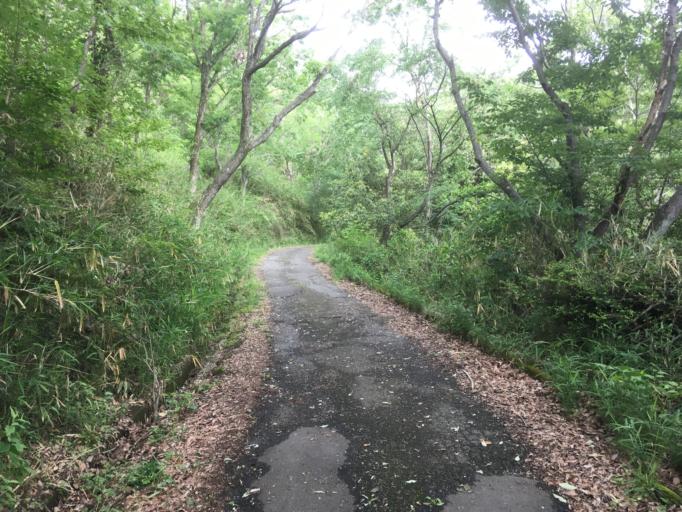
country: JP
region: Nara
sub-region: Ikoma-shi
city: Ikoma
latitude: 34.6847
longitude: 135.6743
